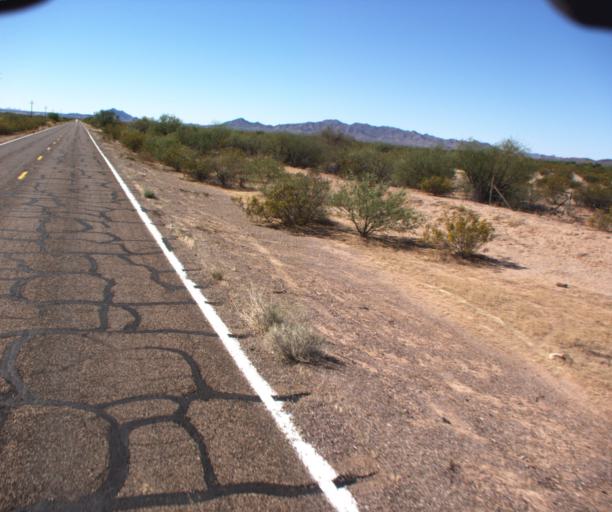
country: US
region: Arizona
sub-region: Pima County
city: Ajo
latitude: 32.4755
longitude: -112.8774
